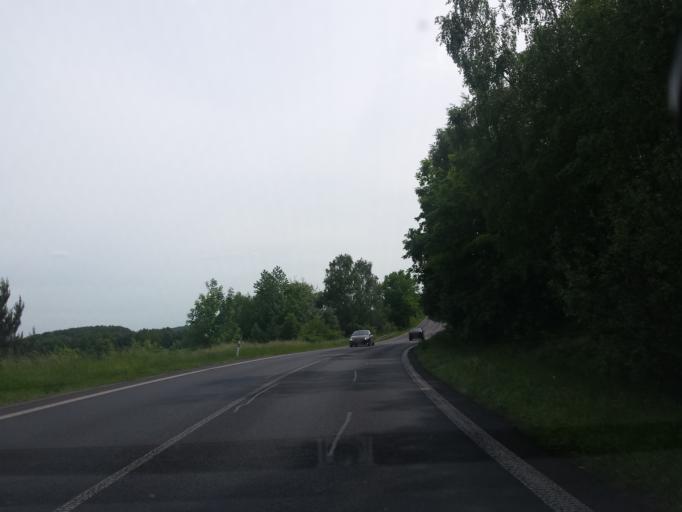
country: CZ
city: Novy Bor
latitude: 50.7399
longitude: 14.5515
